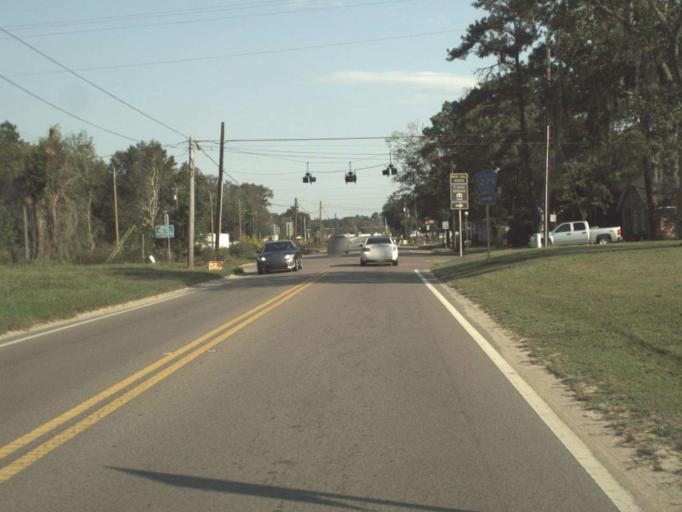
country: US
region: Florida
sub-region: Holmes County
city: Bonifay
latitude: 30.6206
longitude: -85.7124
